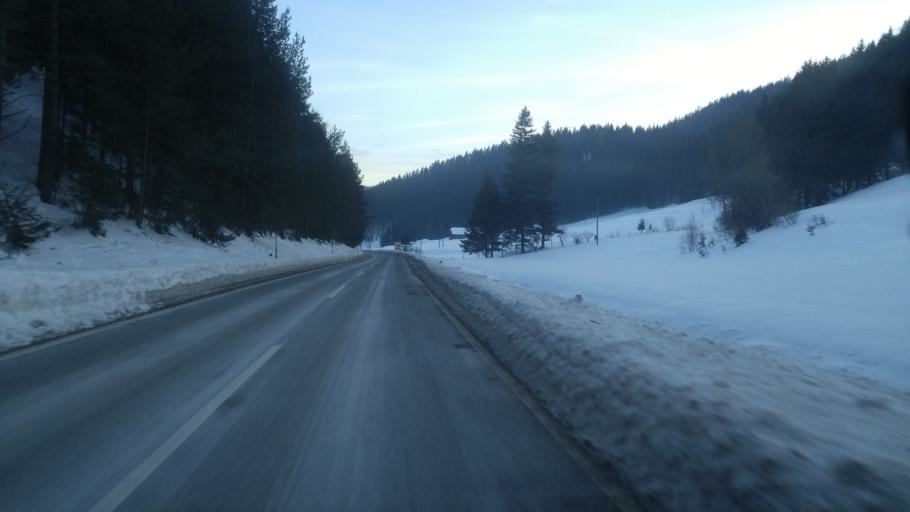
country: AT
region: Lower Austria
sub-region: Politischer Bezirk Wiener Neustadt
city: Rohr im Gebirge
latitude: 47.8761
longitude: 15.6962
